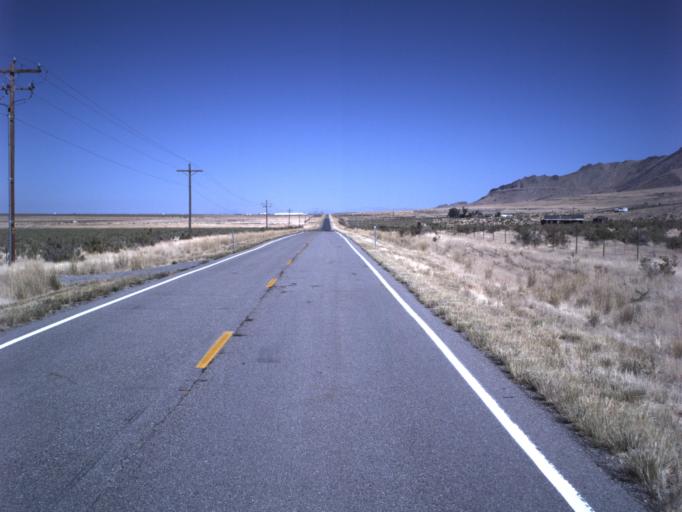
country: US
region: Utah
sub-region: Tooele County
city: Grantsville
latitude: 40.6753
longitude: -112.6727
